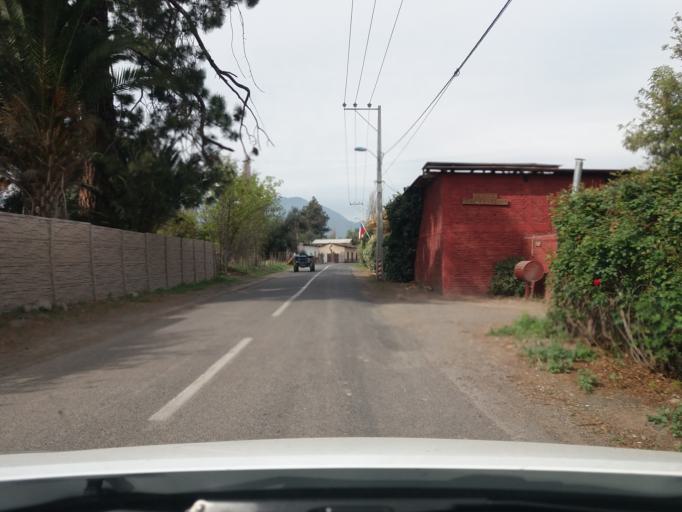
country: CL
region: Valparaiso
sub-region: Provincia de Los Andes
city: Los Andes
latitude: -32.8356
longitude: -70.6602
